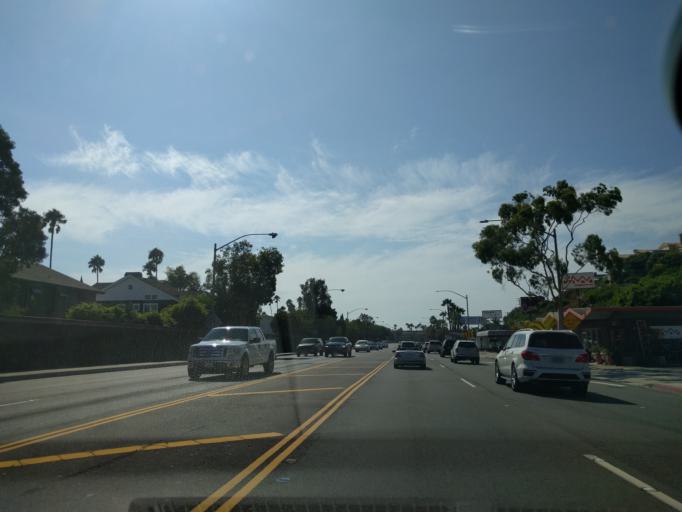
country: US
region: California
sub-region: Orange County
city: Newport Beach
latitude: 33.6161
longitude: -117.9084
